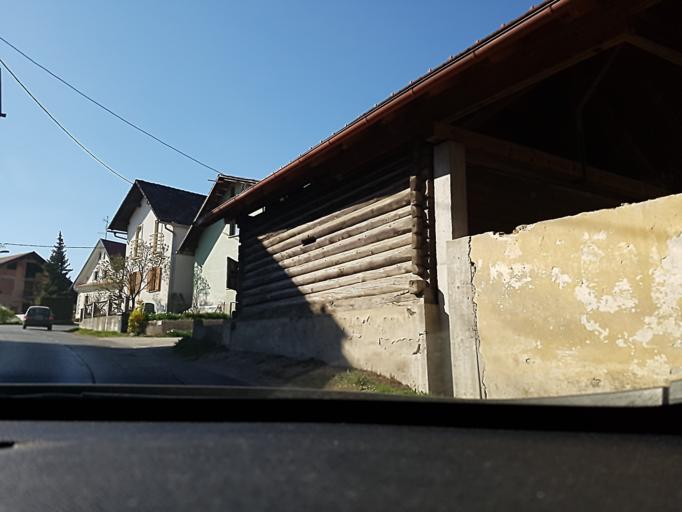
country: SI
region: Trzin
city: Trzin
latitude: 46.1225
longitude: 14.5035
